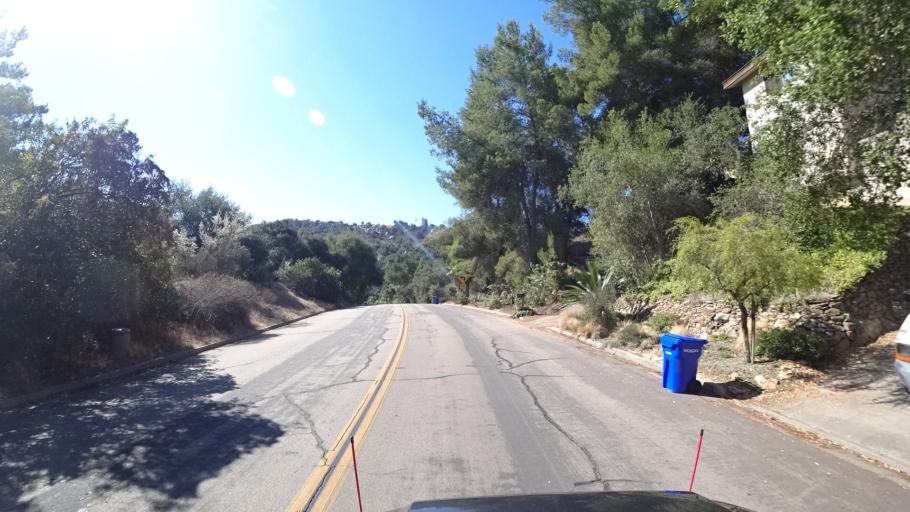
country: US
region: California
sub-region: San Diego County
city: Hidden Meadows
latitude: 33.2167
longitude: -117.1187
